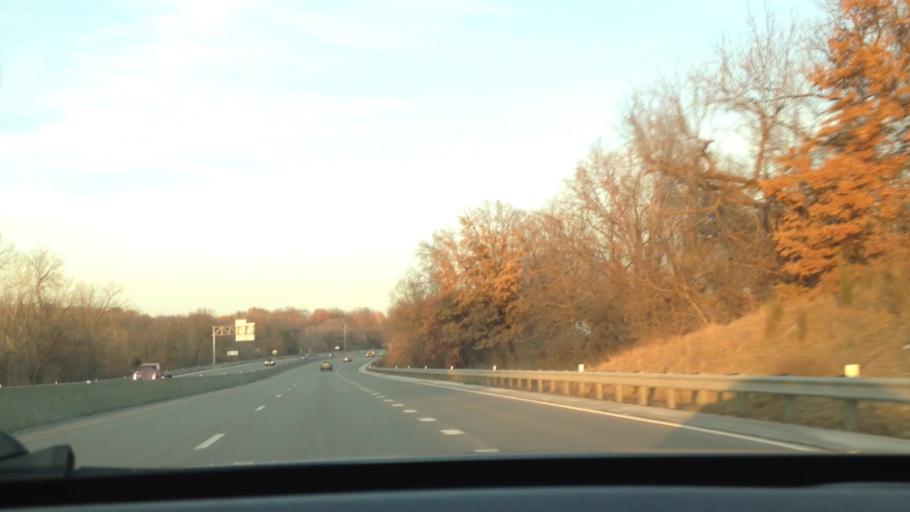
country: US
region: Missouri
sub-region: Clay County
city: Claycomo
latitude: 39.1986
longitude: -94.5097
